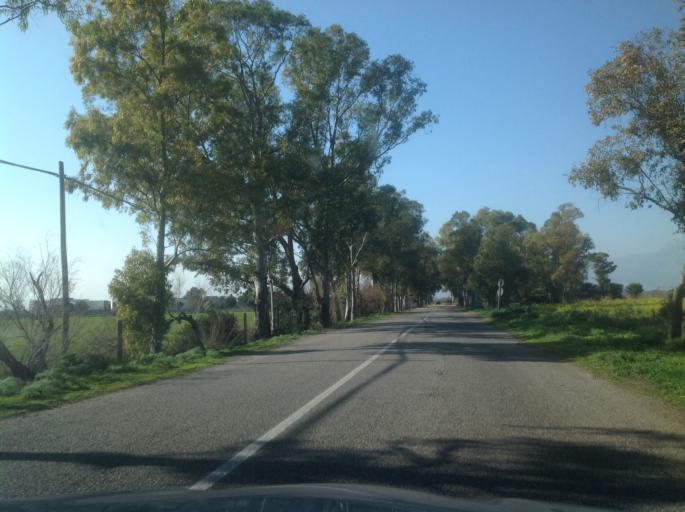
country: IT
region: Calabria
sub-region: Provincia di Cosenza
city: Sibari
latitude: 39.7257
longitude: 16.4995
